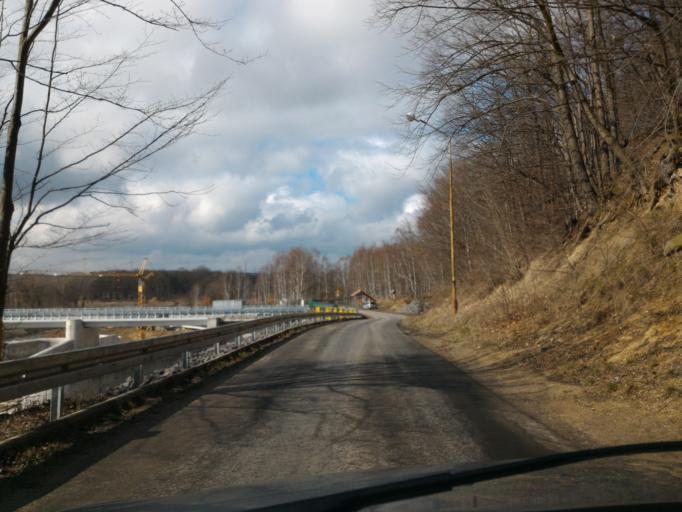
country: DE
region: Saxony
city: Ostritz
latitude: 51.0426
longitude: 14.9840
